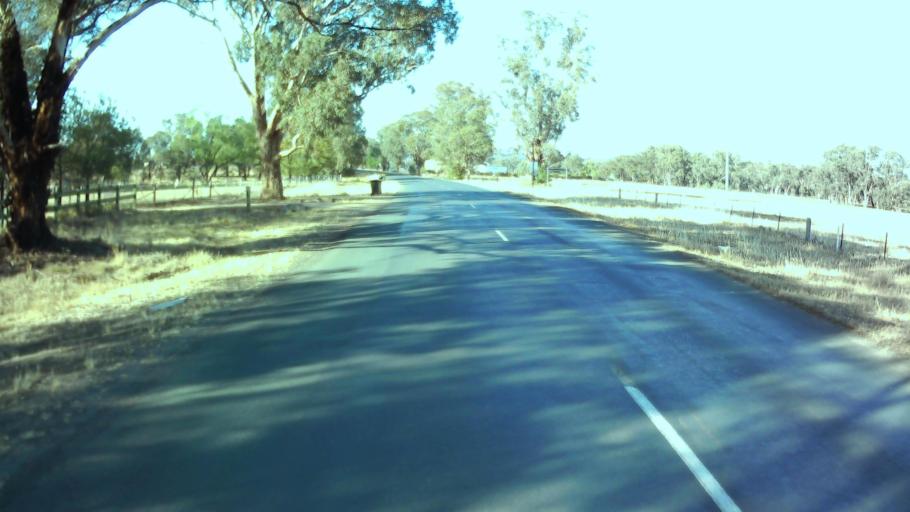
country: AU
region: New South Wales
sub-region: Weddin
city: Grenfell
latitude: -33.9028
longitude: 148.1501
